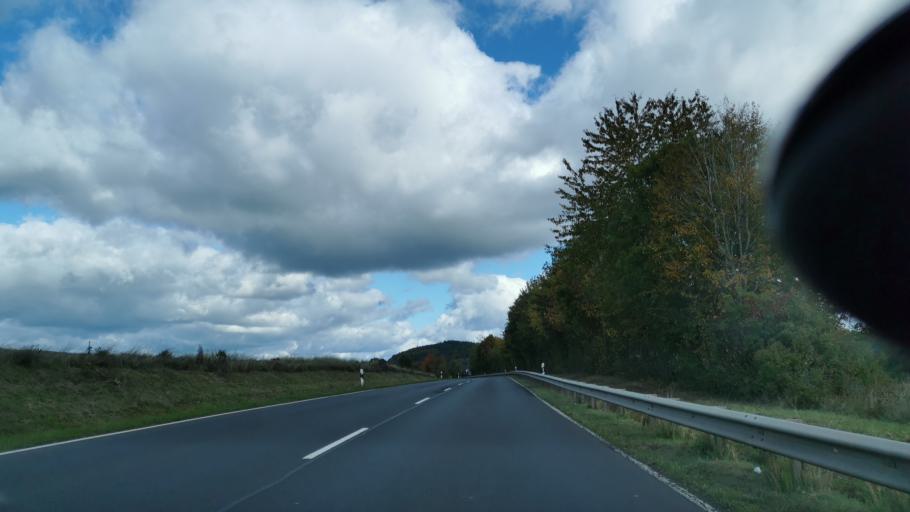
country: DE
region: Rheinland-Pfalz
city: Walsdorf
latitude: 50.3031
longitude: 6.7233
